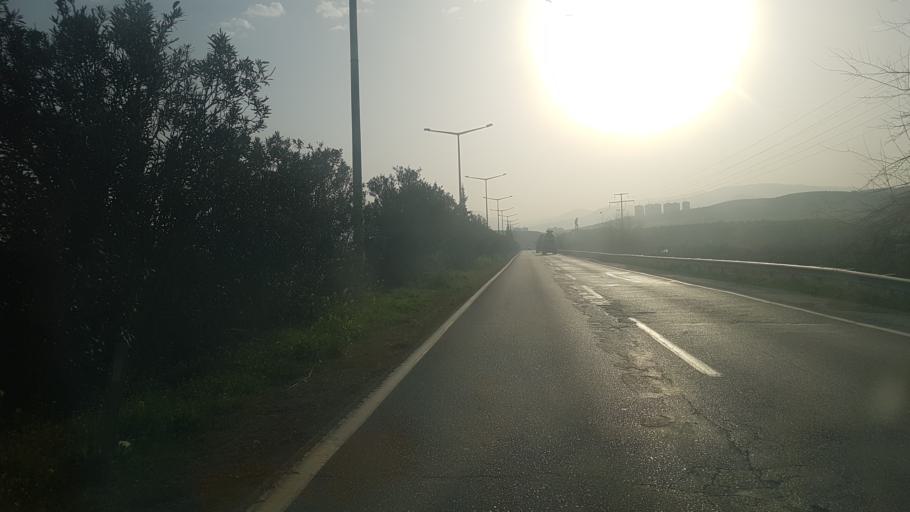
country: TR
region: Osmaniye
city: Toprakkale
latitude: 37.0534
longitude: 36.1433
